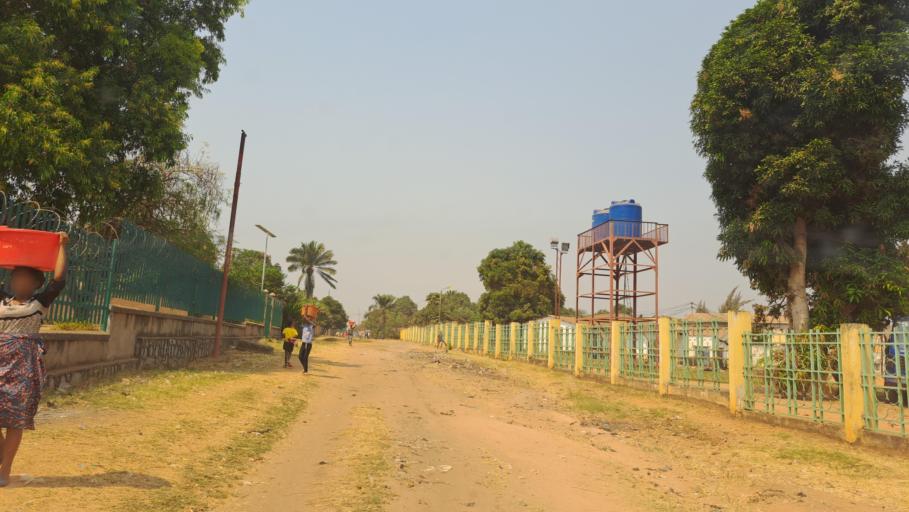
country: CD
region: Kasai-Oriental
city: Mbuji-Mayi
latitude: -6.1103
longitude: 23.5951
